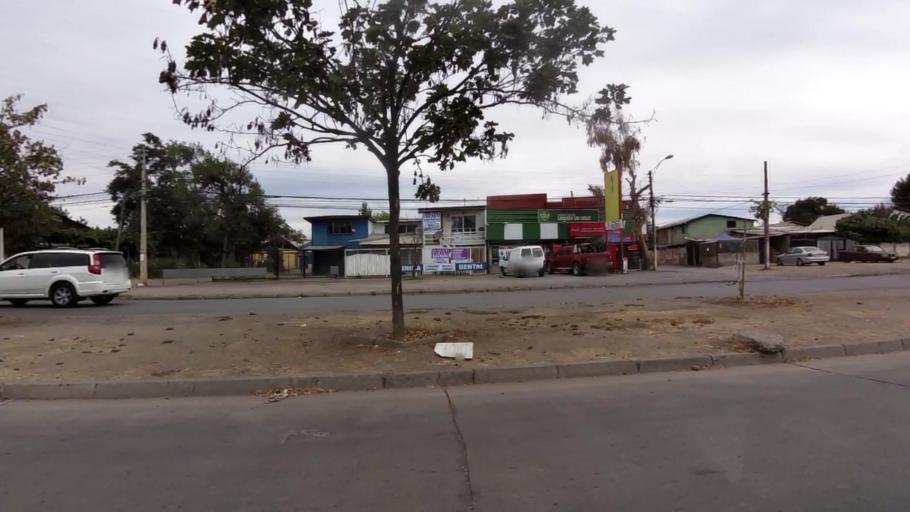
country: CL
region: O'Higgins
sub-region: Provincia de Cachapoal
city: Rancagua
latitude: -34.1458
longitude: -70.7333
